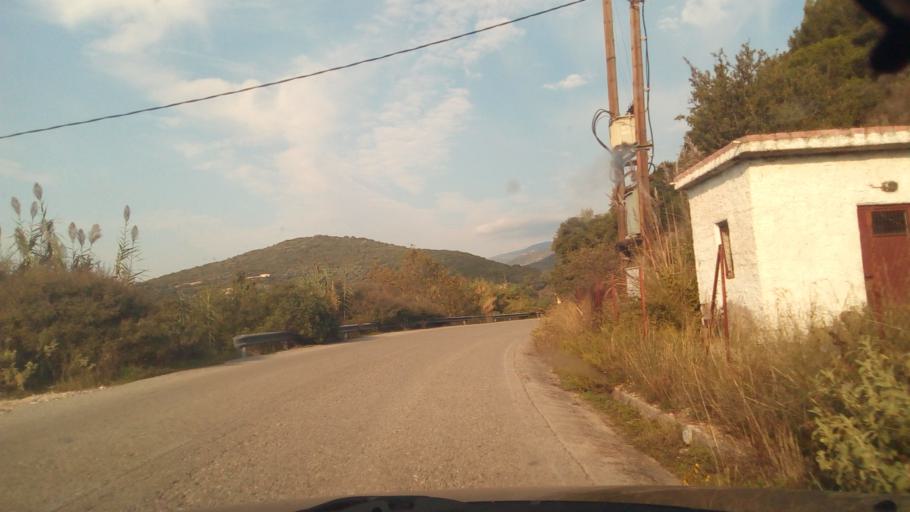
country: GR
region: West Greece
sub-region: Nomos Aitolias kai Akarnanias
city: Nafpaktos
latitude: 38.4229
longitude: 21.9175
